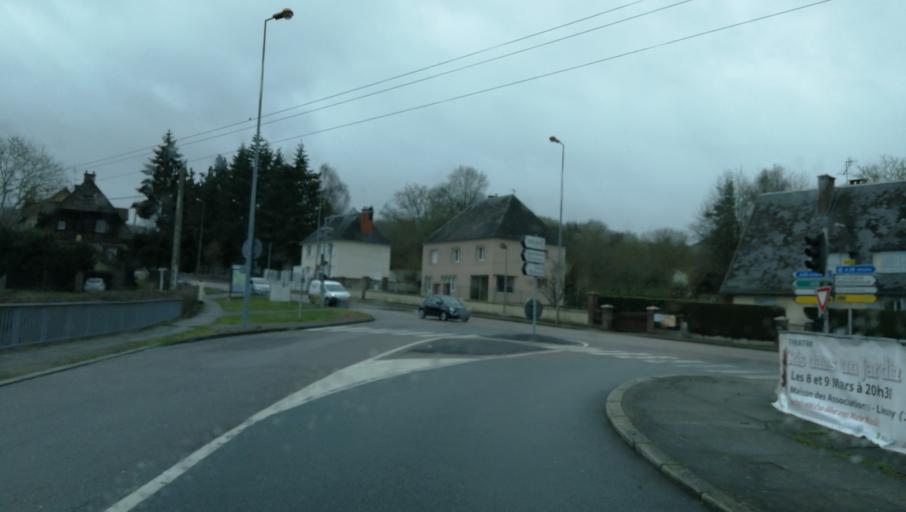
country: FR
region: Haute-Normandie
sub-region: Departement de l'Eure
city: Brionne
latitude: 49.1921
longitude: 0.7117
